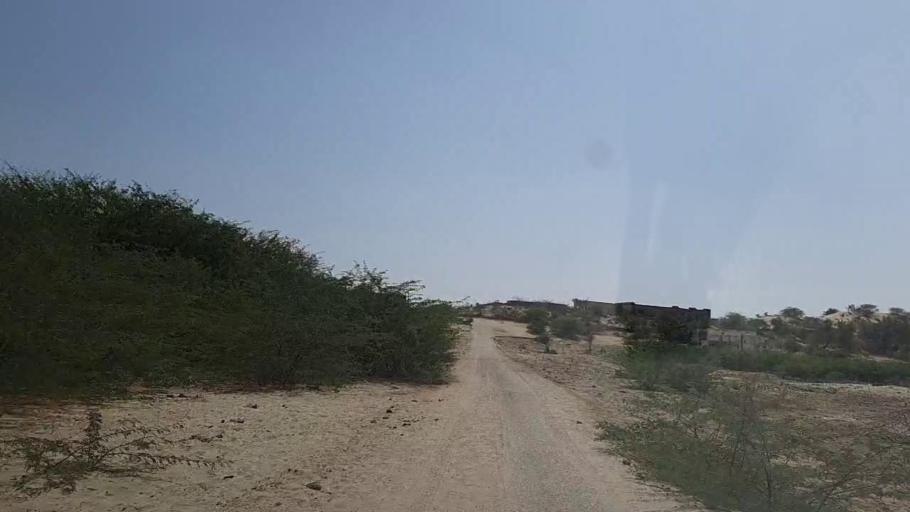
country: PK
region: Sindh
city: Diplo
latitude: 24.5115
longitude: 69.4140
